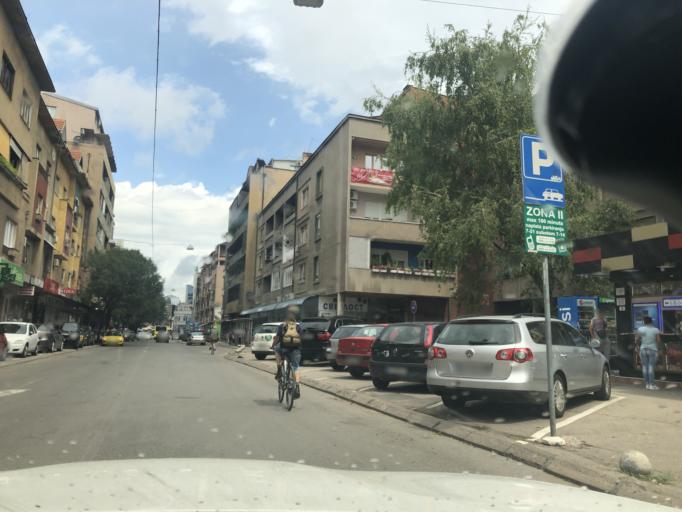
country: RS
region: Central Serbia
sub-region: Nisavski Okrug
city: Nis
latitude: 43.3150
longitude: 21.8946
